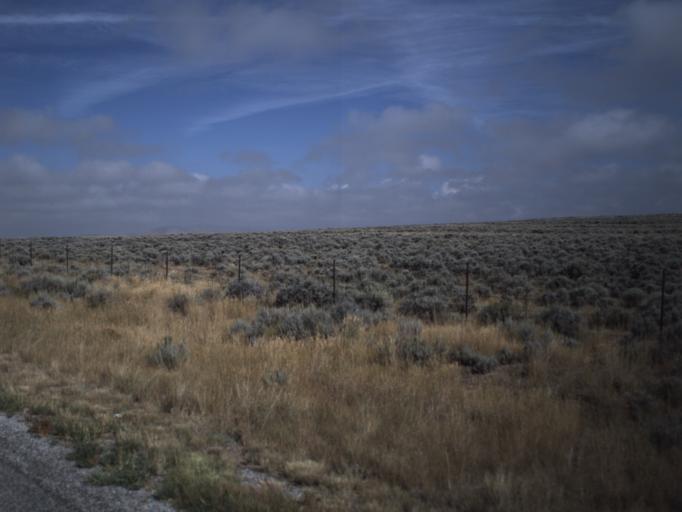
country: US
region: Wyoming
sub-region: Uinta County
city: Evanston
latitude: 41.4372
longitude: -111.0688
